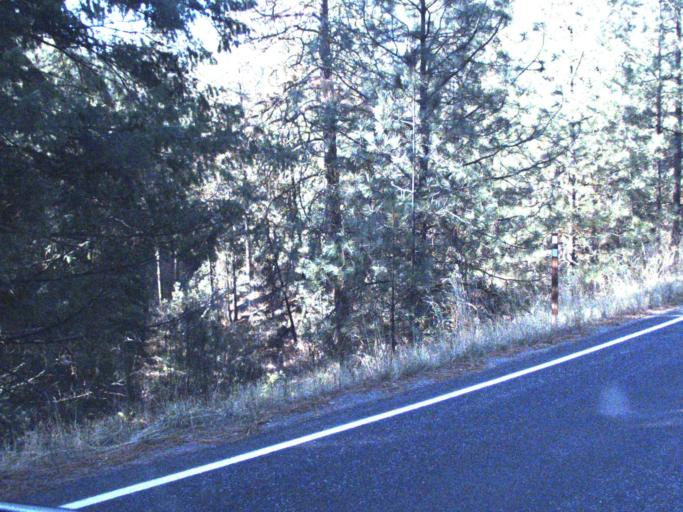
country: US
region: Washington
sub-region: Stevens County
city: Kettle Falls
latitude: 48.1887
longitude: -118.1708
